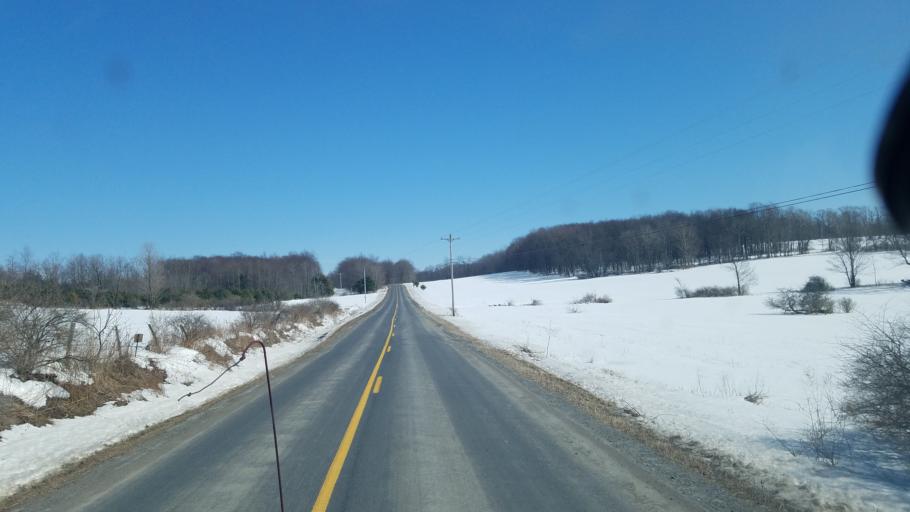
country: US
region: New York
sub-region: Allegany County
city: Andover
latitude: 42.0949
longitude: -77.7208
